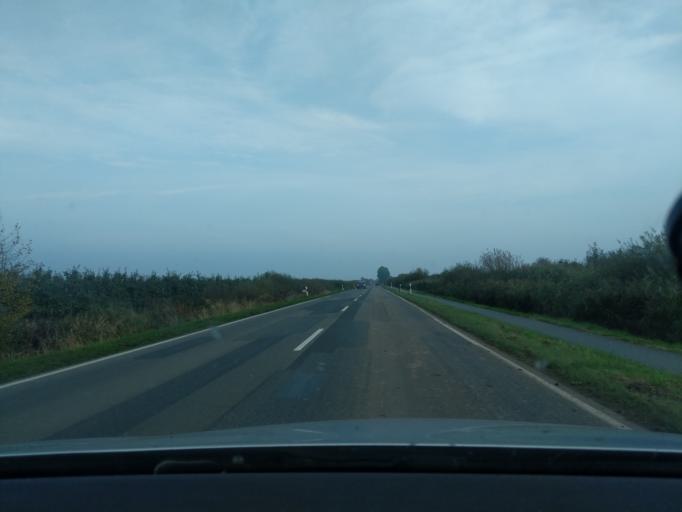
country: DE
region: Lower Saxony
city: Guderhandviertel
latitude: 53.5450
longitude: 9.5927
